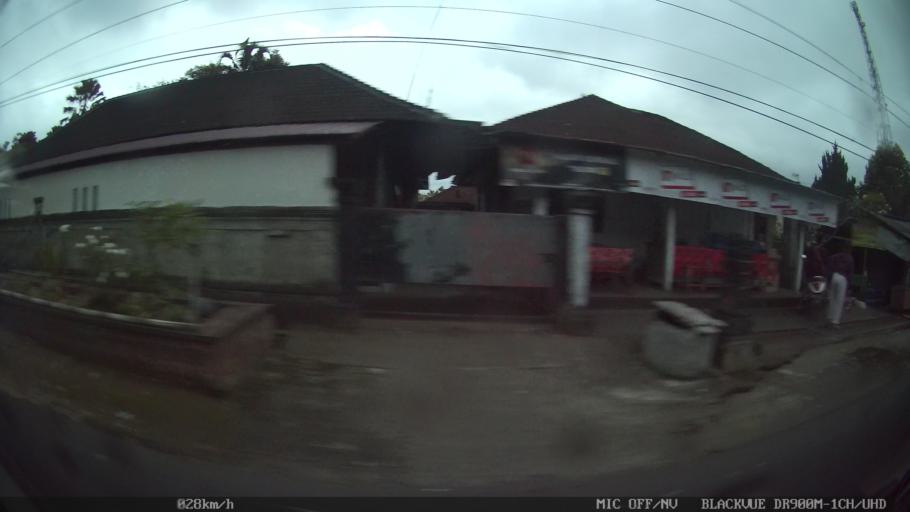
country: ID
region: Bali
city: Banjar Buahan
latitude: -8.4090
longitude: 115.2453
